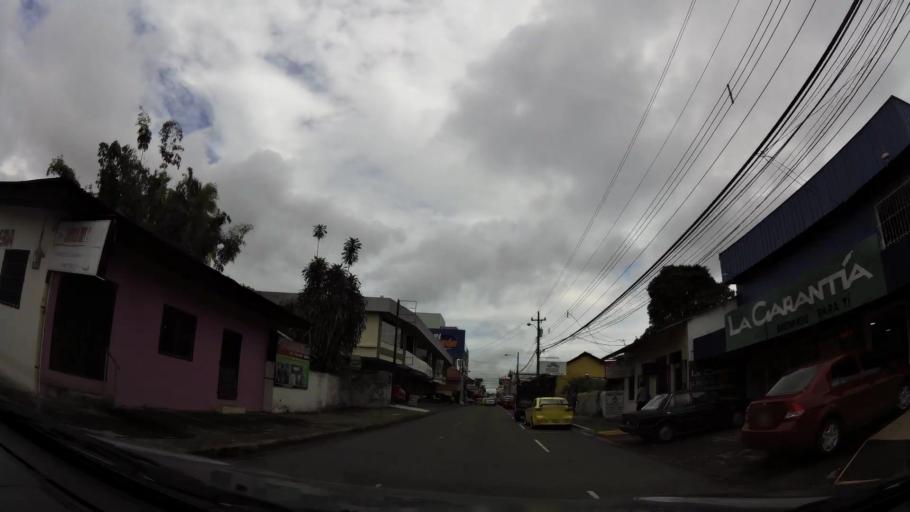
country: PA
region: Chiriqui
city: David
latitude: 8.4254
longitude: -82.4272
